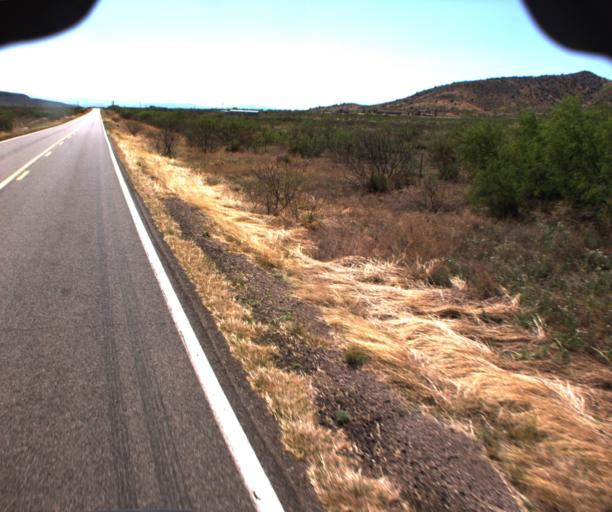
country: US
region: Arizona
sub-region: Cochise County
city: Douglas
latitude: 31.4899
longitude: -109.4225
